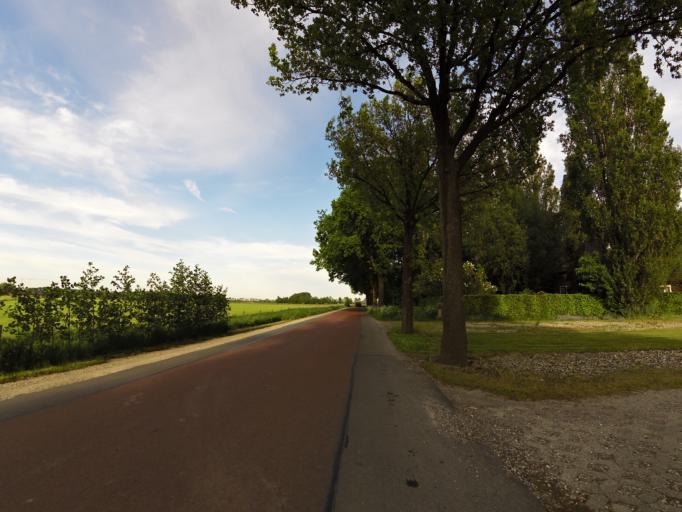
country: NL
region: Gelderland
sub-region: Gemeente Montferland
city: s-Heerenberg
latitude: 51.8858
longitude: 6.3138
